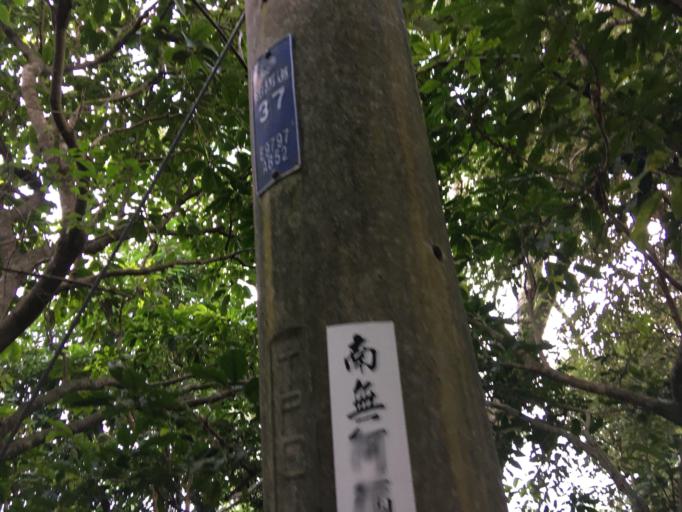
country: TW
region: Taiwan
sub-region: Yilan
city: Yilan
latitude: 24.8422
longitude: 121.7766
